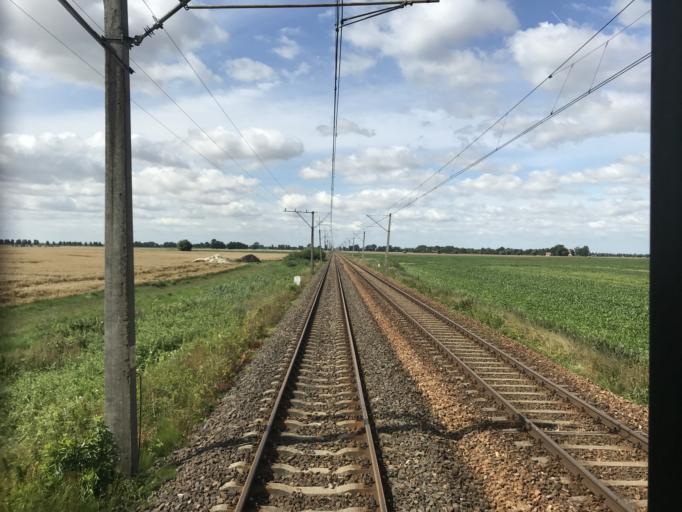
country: PL
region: Warmian-Masurian Voivodeship
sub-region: Powiat elblaski
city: Gronowo Elblaskie
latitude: 54.0768
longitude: 19.2725
